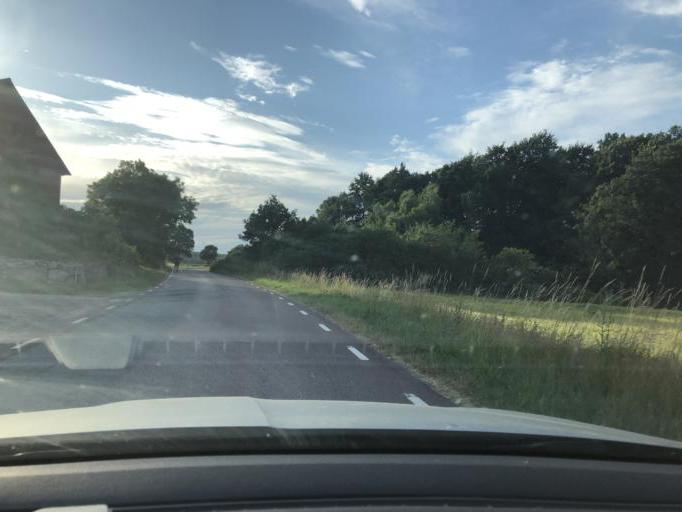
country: SE
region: Blekinge
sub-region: Solvesborgs Kommun
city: Soelvesborg
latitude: 56.1192
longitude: 14.6204
